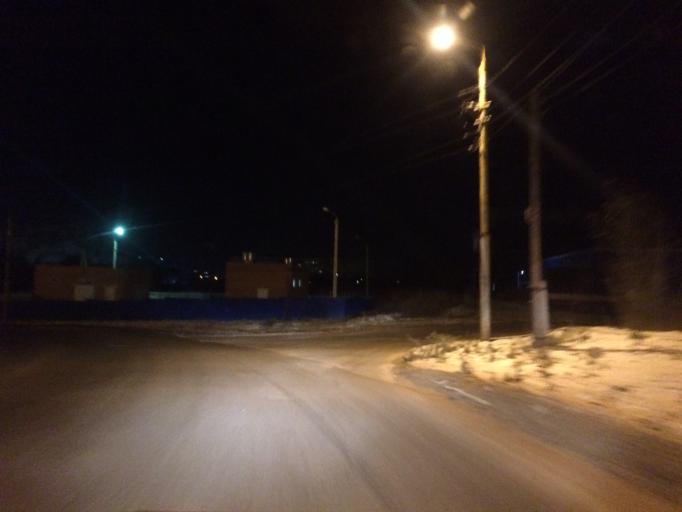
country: RU
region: Tula
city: Mendeleyevskiy
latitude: 54.1531
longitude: 37.6041
